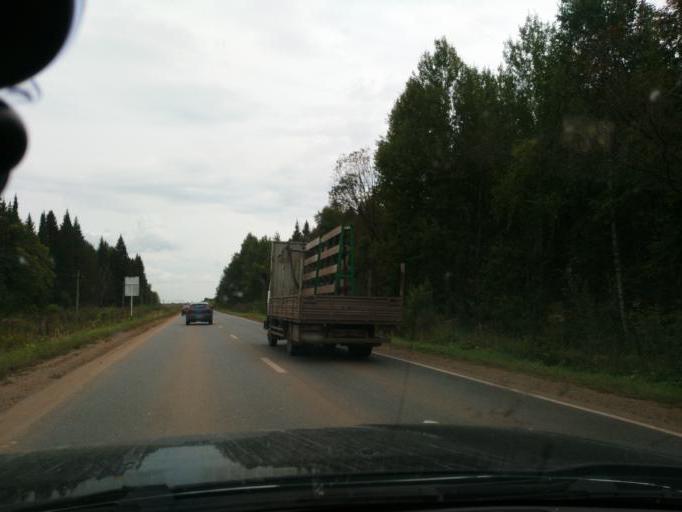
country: RU
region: Perm
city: Chernushka
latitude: 56.5101
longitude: 55.9377
